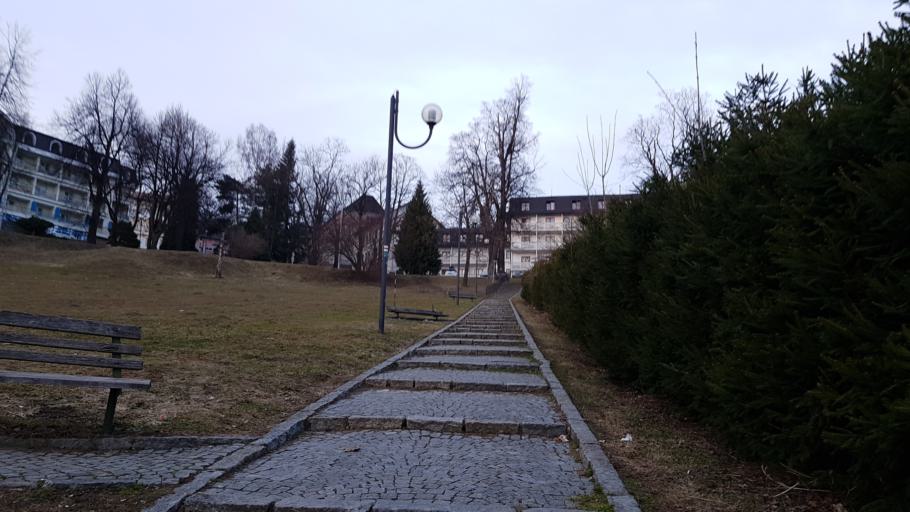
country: CZ
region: Olomoucky
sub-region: Okres Jesenik
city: Jesenik
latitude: 50.2390
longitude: 17.1868
